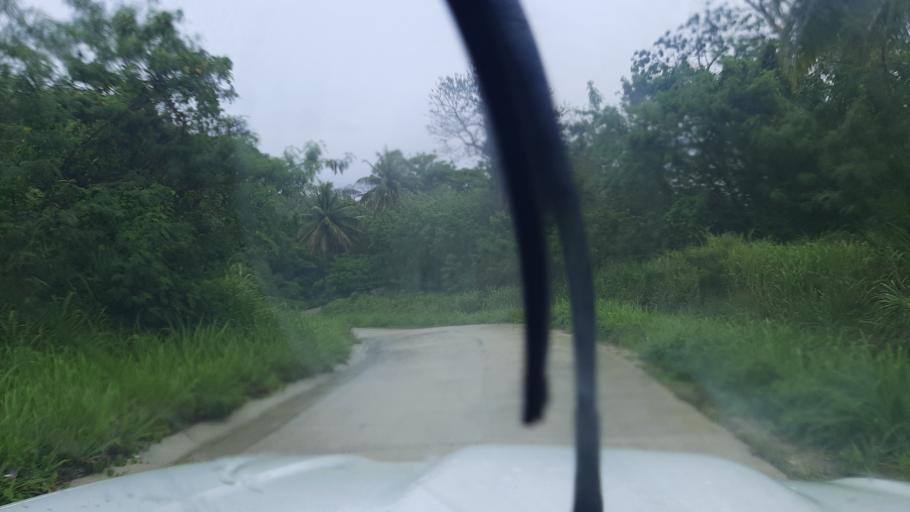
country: VU
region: Shefa
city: Port-Vila
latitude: -17.6364
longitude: 168.2089
